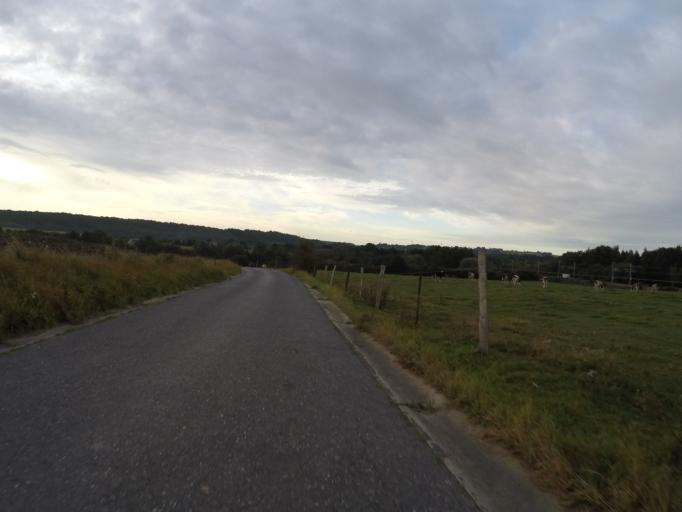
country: BE
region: Wallonia
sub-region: Province de Namur
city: Ciney
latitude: 50.3312
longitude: 5.0652
